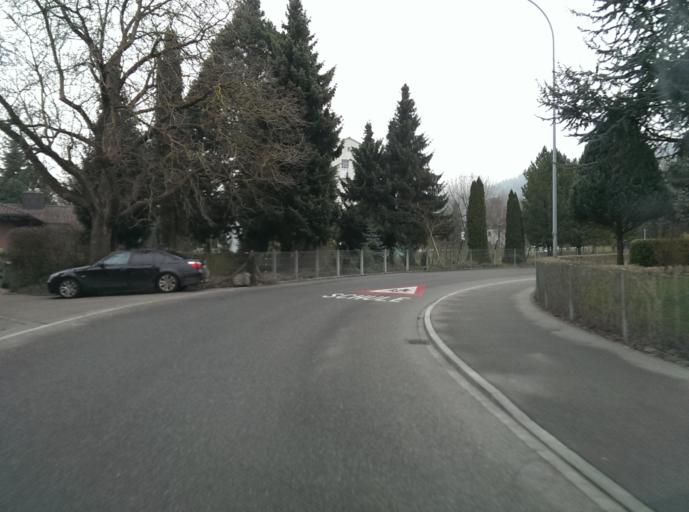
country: CH
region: Aargau
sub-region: Bezirk Baden
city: Neuenhof
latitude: 47.4472
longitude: 8.3326
